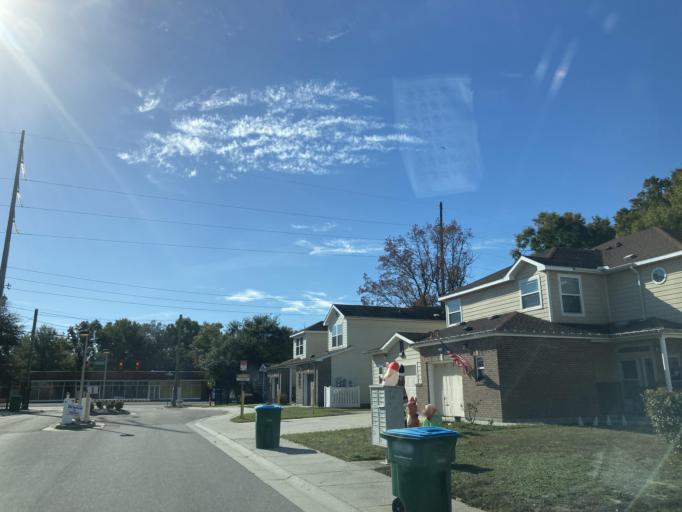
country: US
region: Mississippi
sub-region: Harrison County
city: D'Iberville
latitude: 30.4040
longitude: -88.9504
